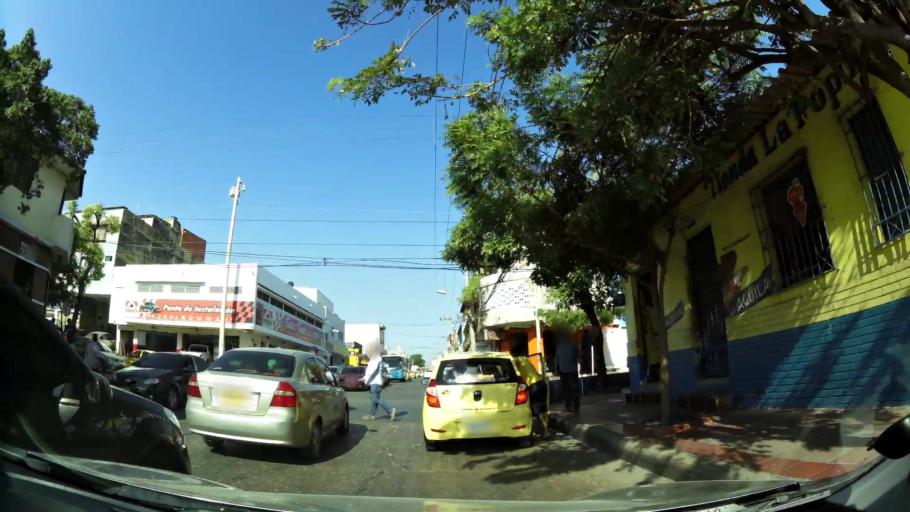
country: CO
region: Atlantico
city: Barranquilla
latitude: 10.9801
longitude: -74.7880
